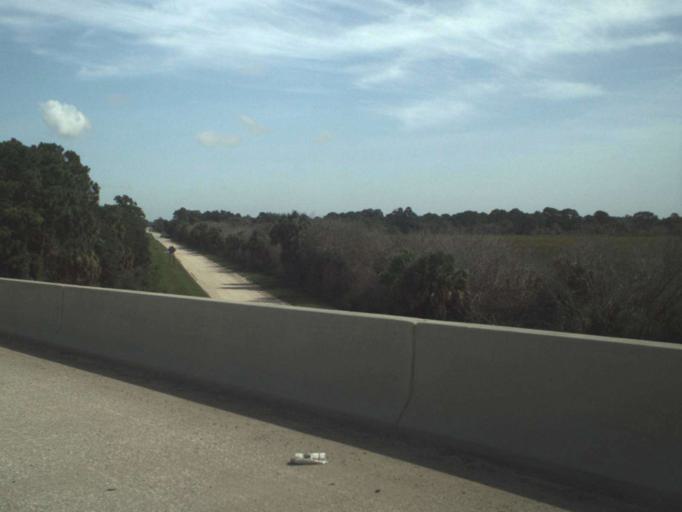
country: US
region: Florida
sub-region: Indian River County
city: West Vero Corridor
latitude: 27.6119
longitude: -80.5126
